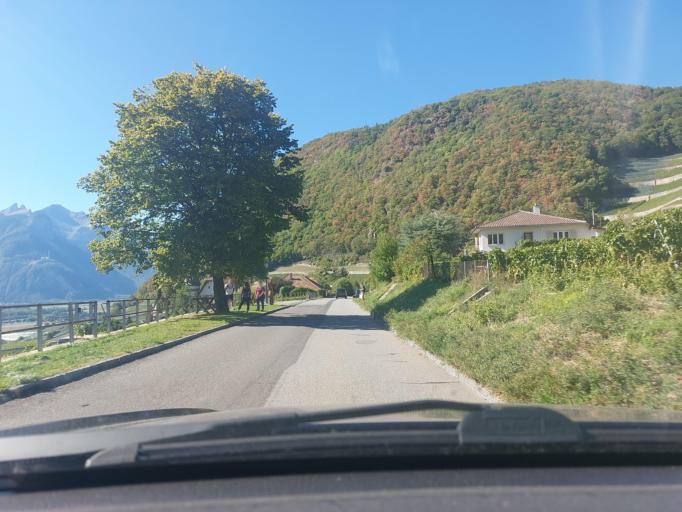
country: CH
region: Vaud
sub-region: Aigle District
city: Aigle
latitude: 46.3340
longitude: 6.9611
